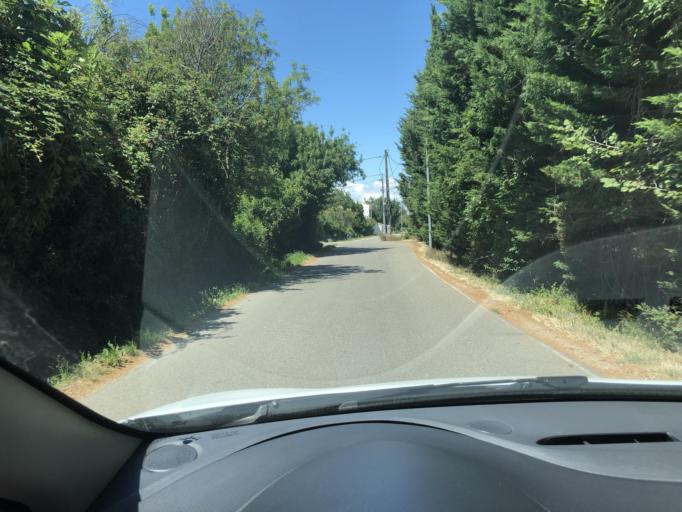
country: FR
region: Provence-Alpes-Cote d'Azur
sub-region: Departement des Bouches-du-Rhone
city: Chateaurenard
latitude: 43.8971
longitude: 4.8672
